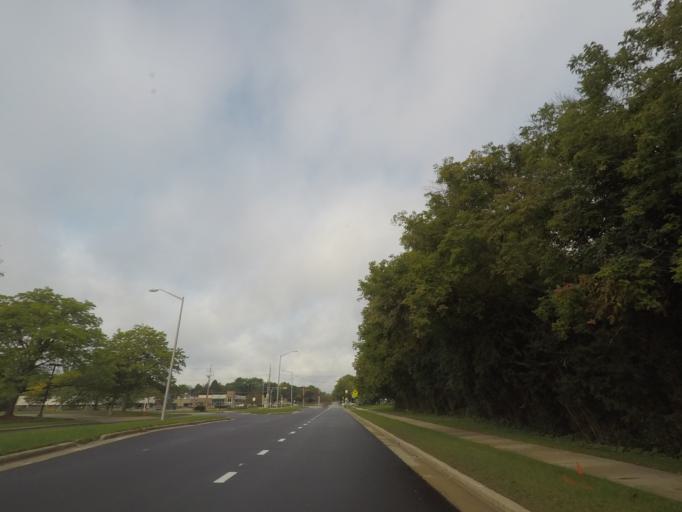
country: US
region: Wisconsin
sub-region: Waukesha County
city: Waukesha
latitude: 43.0250
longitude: -88.2398
